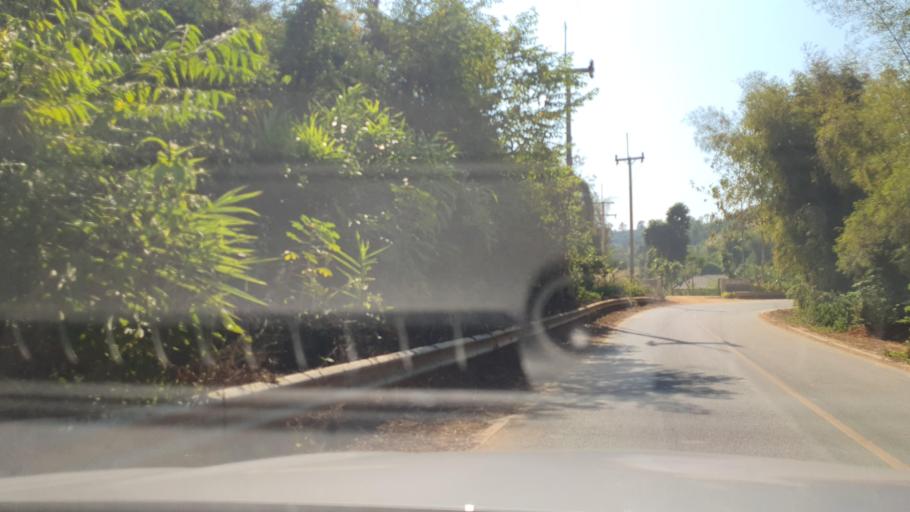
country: TH
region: Nan
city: Pua
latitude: 19.1651
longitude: 100.9099
